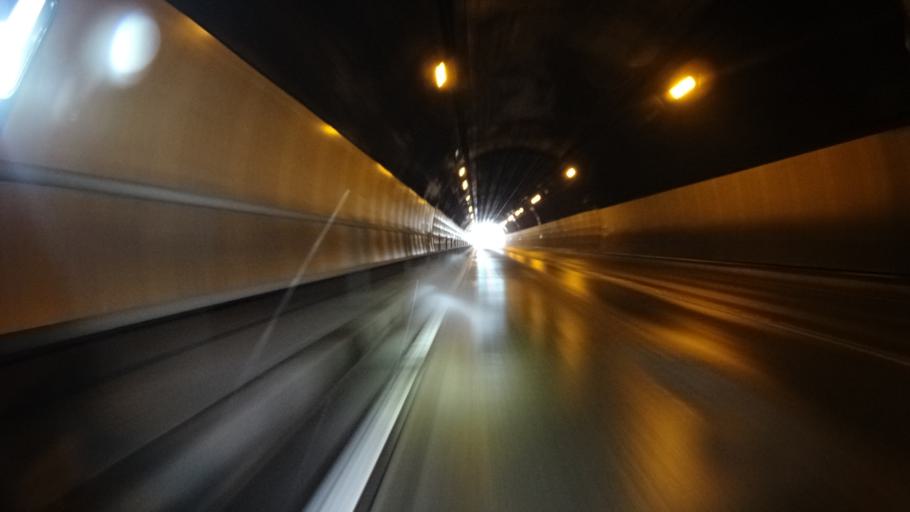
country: JP
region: Tokyo
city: Ome
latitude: 35.8160
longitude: 139.2486
